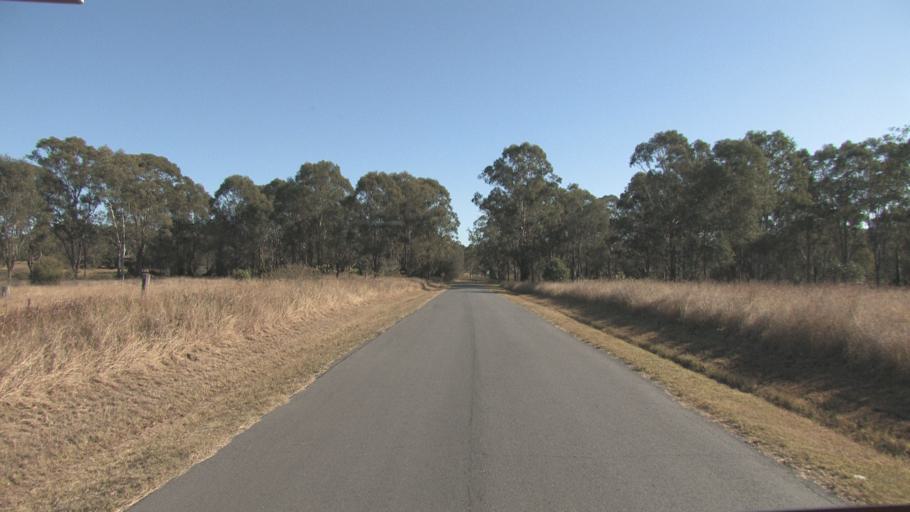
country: AU
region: Queensland
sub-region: Logan
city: North Maclean
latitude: -27.7614
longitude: 153.0466
